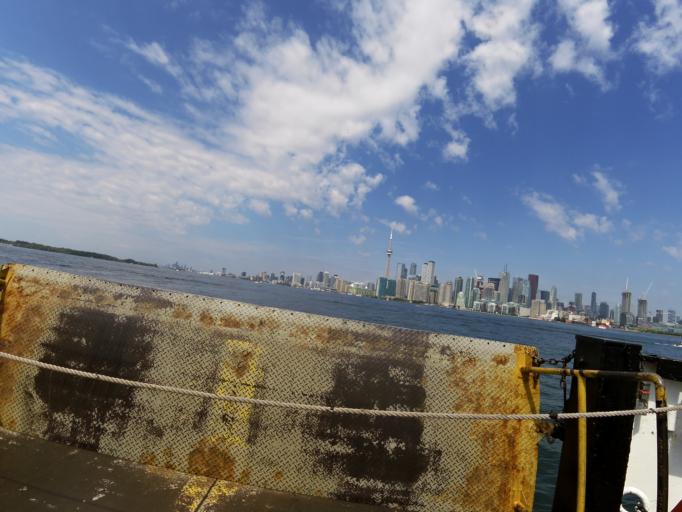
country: CA
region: Ontario
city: Toronto
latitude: 43.6319
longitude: -79.3594
